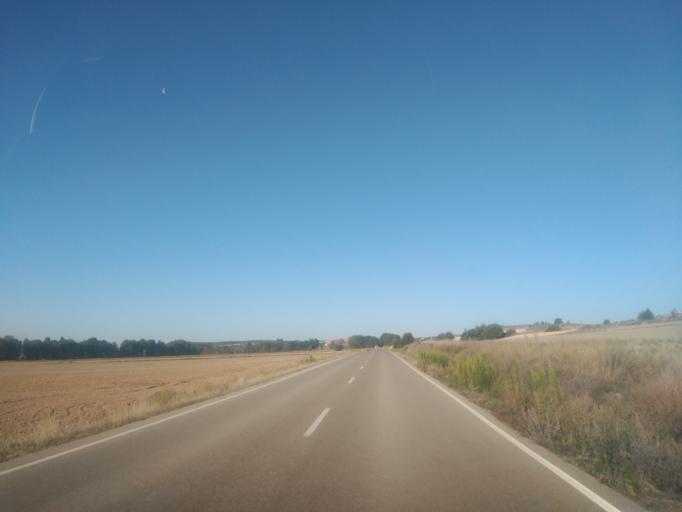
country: ES
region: Castille and Leon
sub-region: Provincia de Burgos
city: Brazacorta
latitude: 41.7192
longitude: -3.3489
